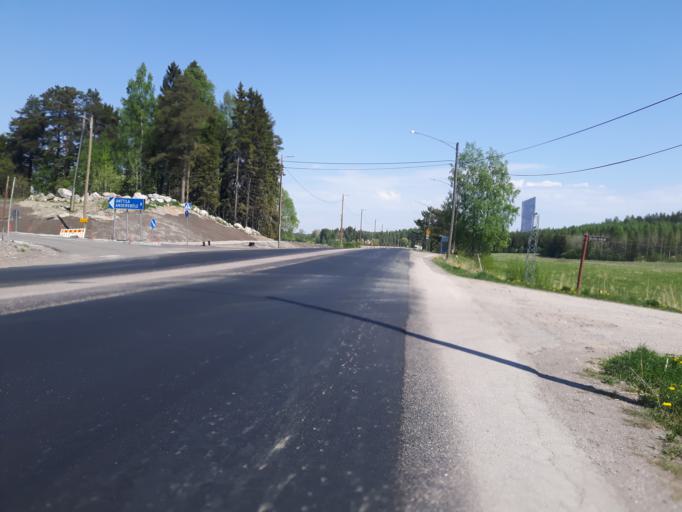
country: FI
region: Uusimaa
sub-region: Porvoo
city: Porvoo
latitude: 60.3493
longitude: 25.4988
